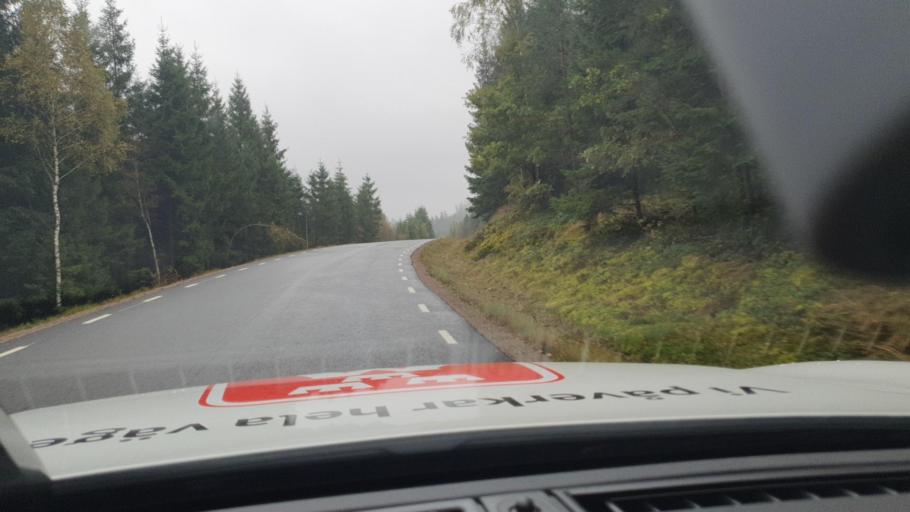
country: SE
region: Vaestra Goetaland
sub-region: Svenljunga Kommun
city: Svenljunga
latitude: 57.3520
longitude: 12.9310
